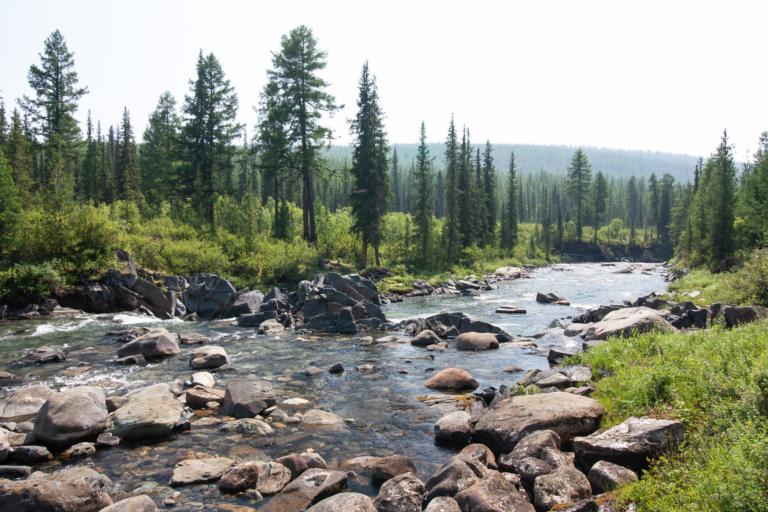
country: RU
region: Respublika Buryatiya
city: Nizhneangarsk
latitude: 56.2109
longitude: 109.7003
